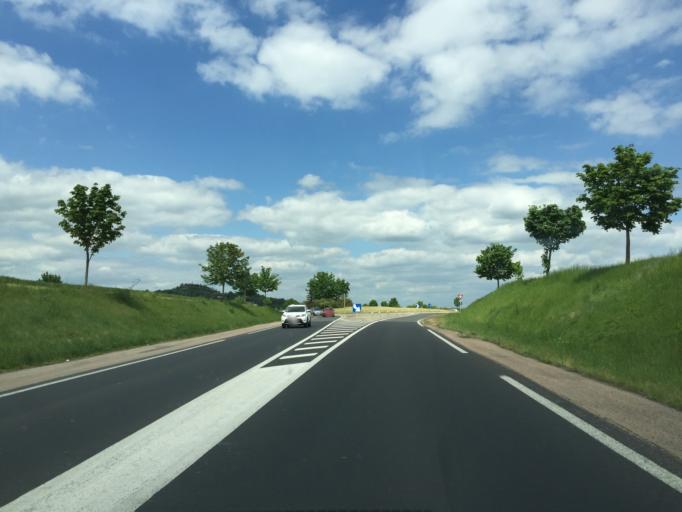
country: FR
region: Auvergne
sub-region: Departement du Puy-de-Dome
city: Aigueperse
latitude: 46.0220
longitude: 3.2164
